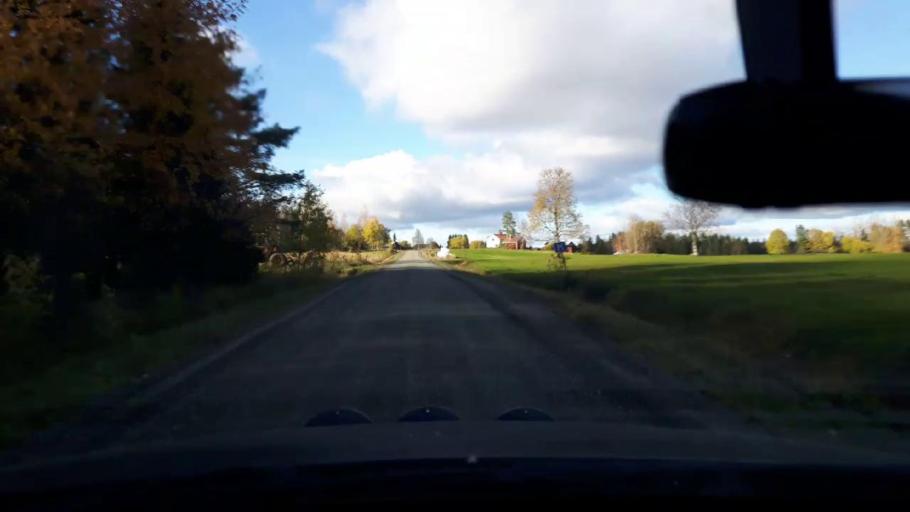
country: SE
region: Jaemtland
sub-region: Bergs Kommun
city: Hoverberg
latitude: 63.0231
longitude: 14.2983
